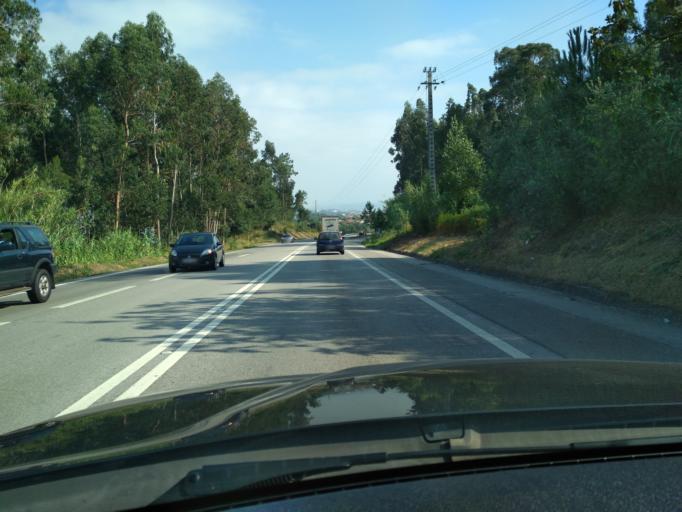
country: PT
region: Aveiro
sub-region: Mealhada
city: Pampilhosa do Botao
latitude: 40.2992
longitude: -8.4465
